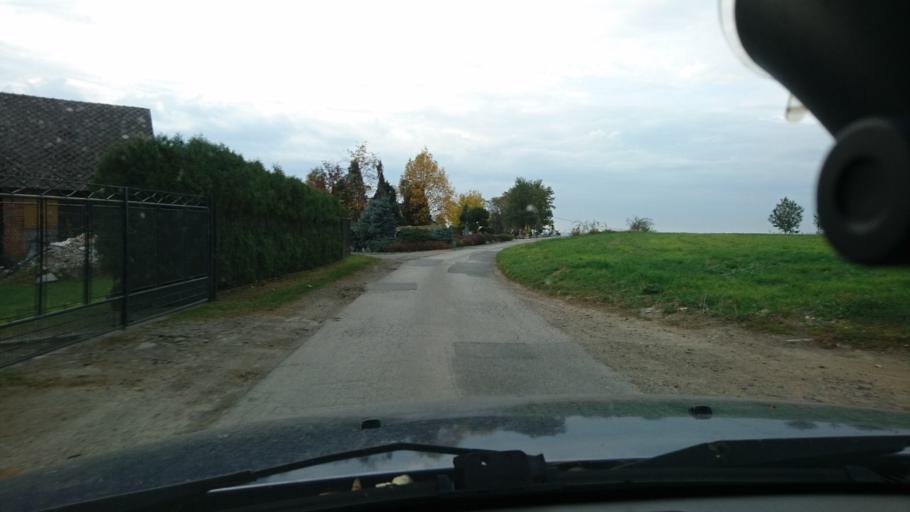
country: PL
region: Silesian Voivodeship
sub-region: Powiat bielski
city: Kozy
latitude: 49.8656
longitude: 19.1549
